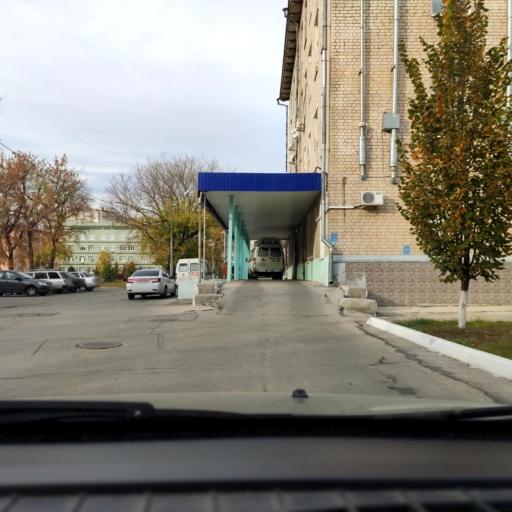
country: RU
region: Samara
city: Tol'yatti
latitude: 53.5024
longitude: 49.4106
